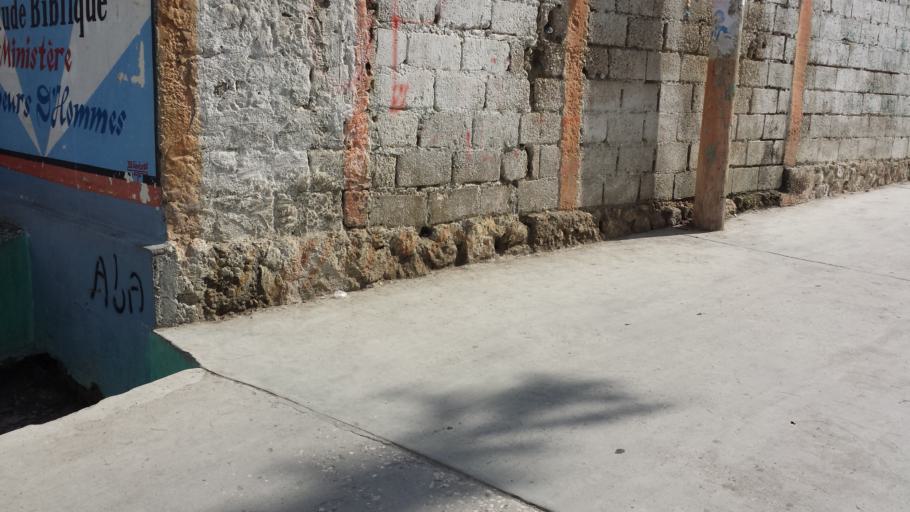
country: HT
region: Artibonite
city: Saint-Marc
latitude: 19.1059
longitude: -72.6943
